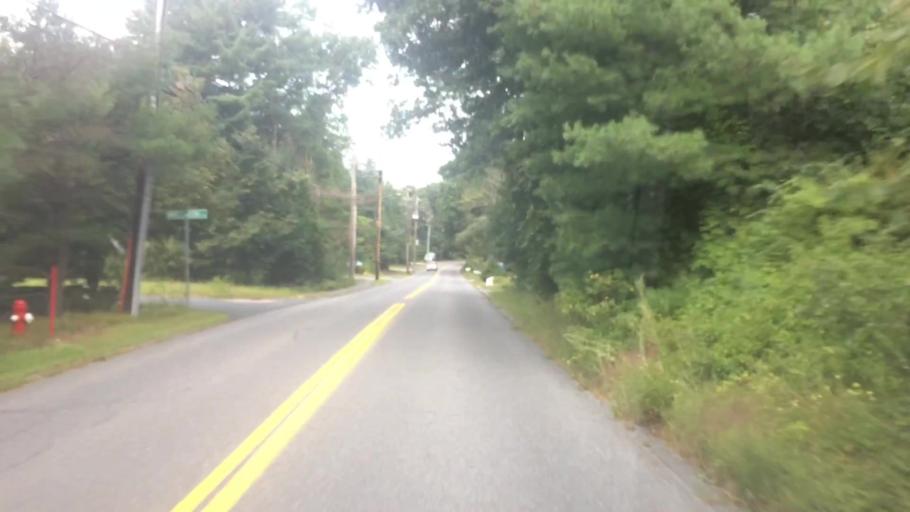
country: US
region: Massachusetts
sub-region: Middlesex County
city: West Concord
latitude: 42.4603
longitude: -71.4158
